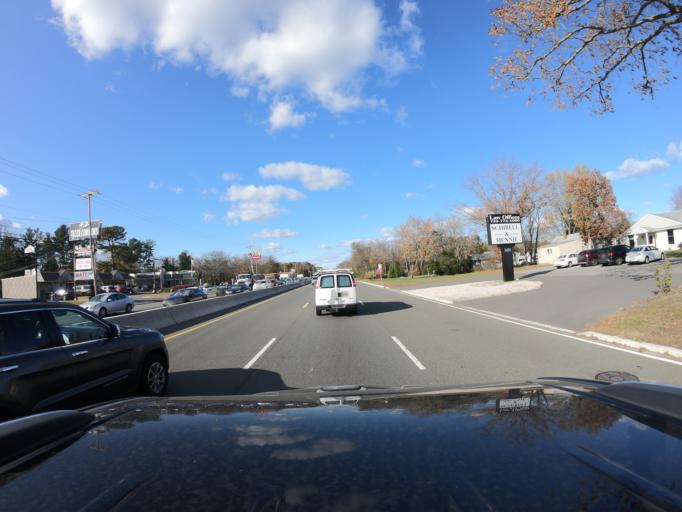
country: US
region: New Jersey
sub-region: Ocean County
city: Lakewood
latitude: 40.1583
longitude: -74.2315
